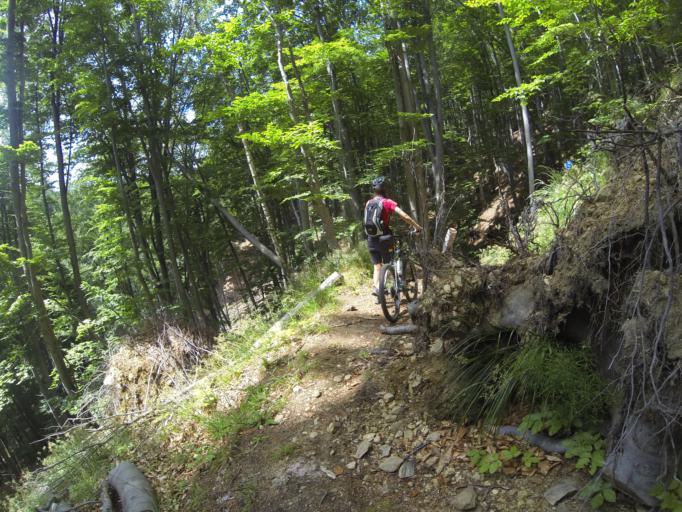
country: RO
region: Valcea
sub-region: Oras Baile Olanesti
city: Cheia
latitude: 45.2284
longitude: 24.1857
